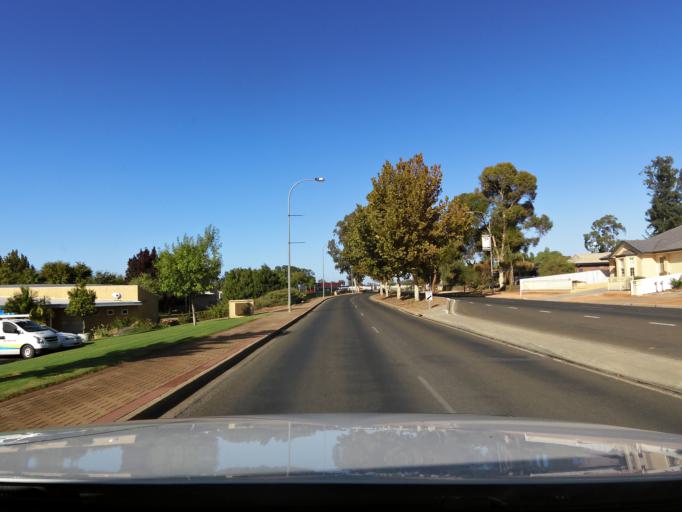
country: AU
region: South Australia
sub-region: Berri and Barmera
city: Berri
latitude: -34.2771
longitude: 140.6101
